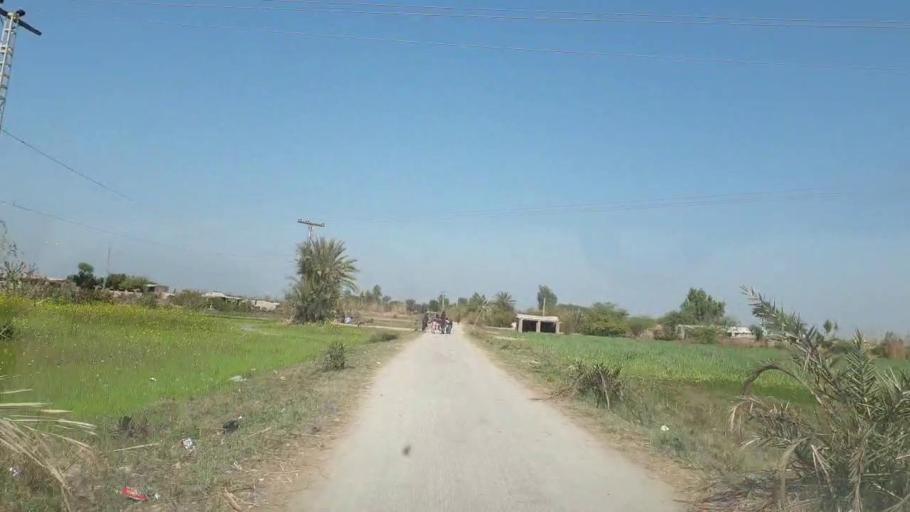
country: PK
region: Sindh
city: Mirpur Khas
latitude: 25.7220
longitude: 69.1172
